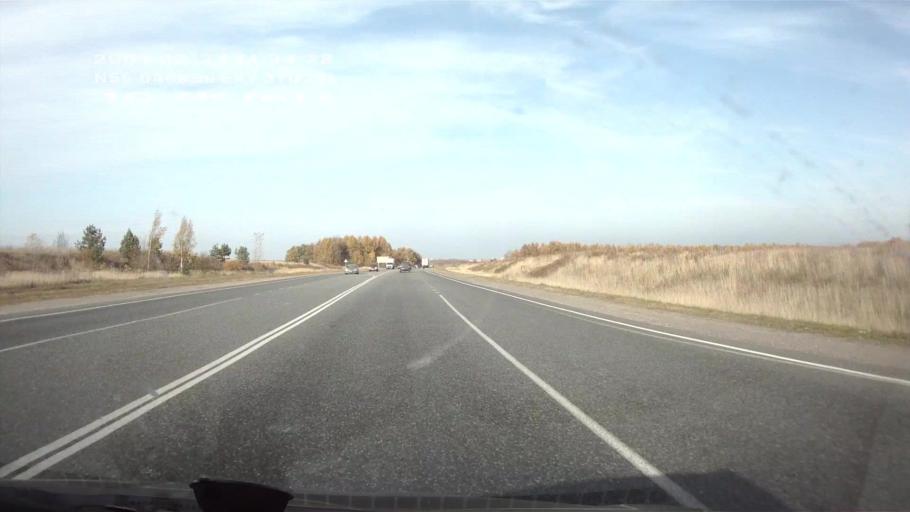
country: RU
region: Chuvashia
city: Kugesi
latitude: 56.0465
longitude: 47.3700
